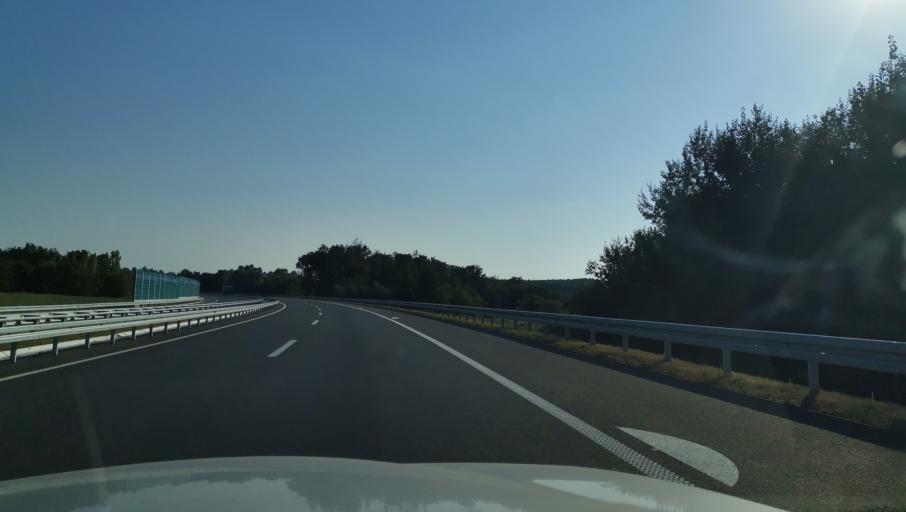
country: RS
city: Stubline
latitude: 44.5113
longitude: 20.1534
